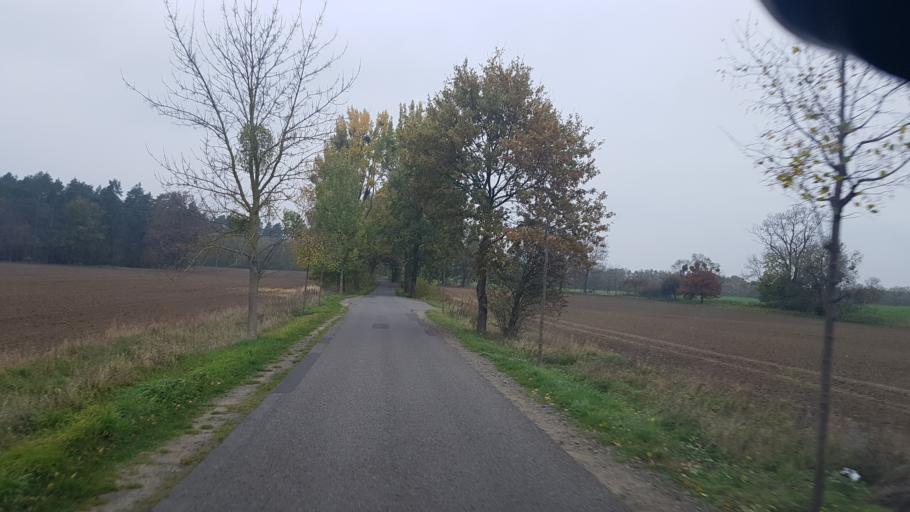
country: DE
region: Brandenburg
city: Lindow
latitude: 52.9443
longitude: 13.0540
